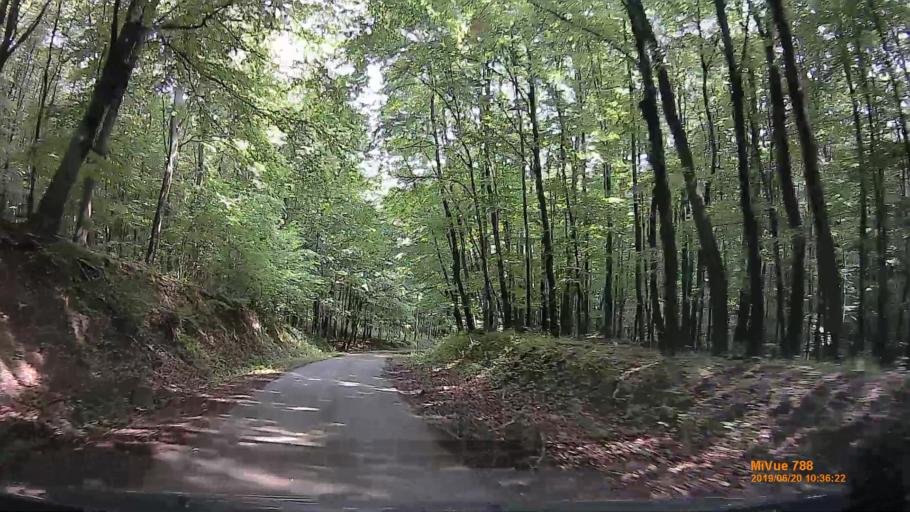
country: HU
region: Baranya
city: Mecseknadasd
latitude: 46.2029
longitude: 18.5302
